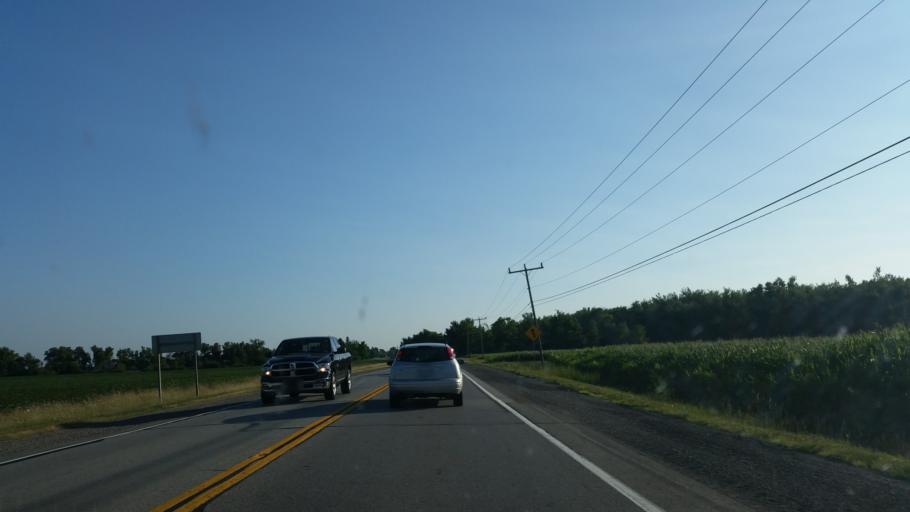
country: CA
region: Ontario
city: Brampton
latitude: 43.8101
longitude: -79.8379
